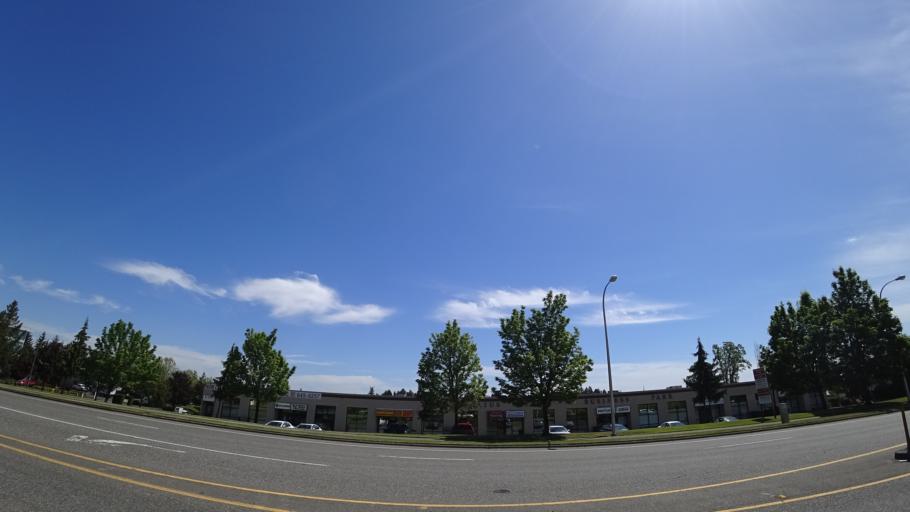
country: US
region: Oregon
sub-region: Washington County
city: Rockcreek
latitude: 45.5341
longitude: -122.8998
